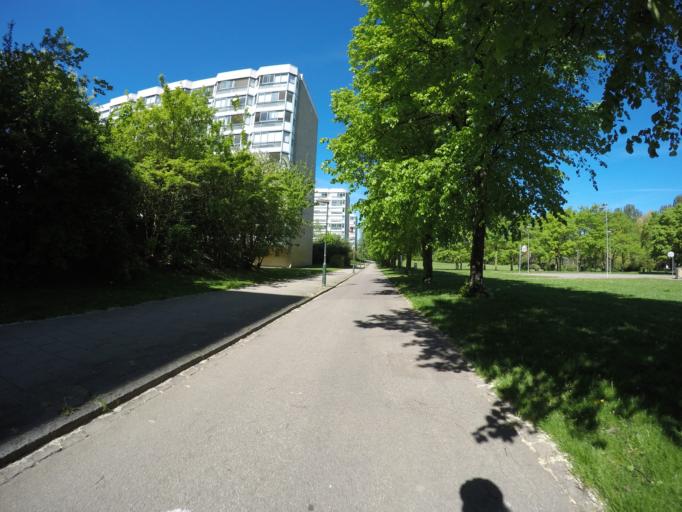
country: SE
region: Skane
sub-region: Malmo
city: Malmoe
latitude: 55.5893
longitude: 13.0473
